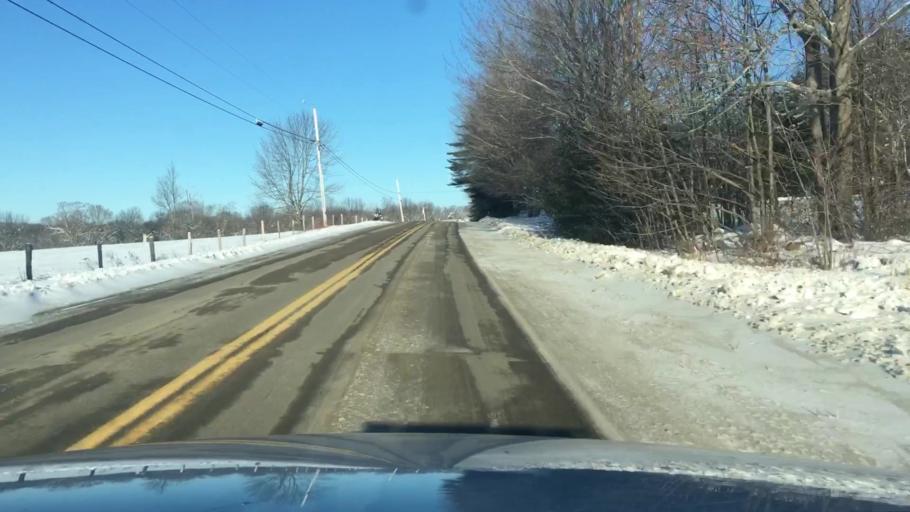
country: US
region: Maine
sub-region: Kennebec County
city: Readfield
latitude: 44.4258
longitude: -69.9335
